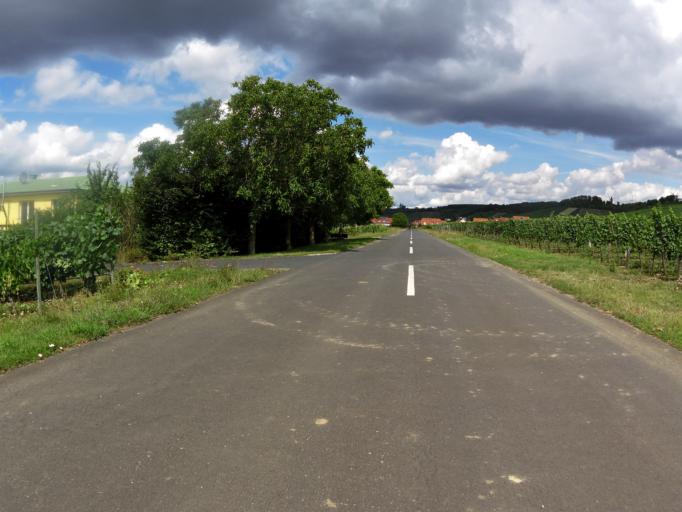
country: DE
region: Bavaria
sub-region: Regierungsbezirk Unterfranken
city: Sommerhausen
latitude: 49.6930
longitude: 10.0275
